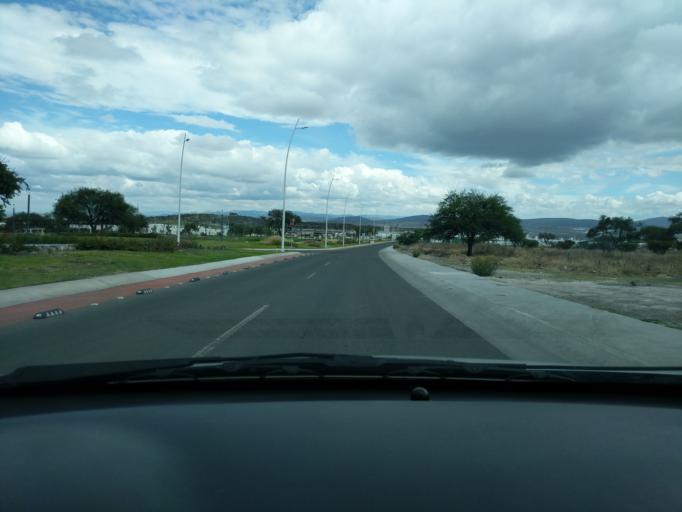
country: MX
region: Queretaro
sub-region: El Marques
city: El Pozo
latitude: 20.6540
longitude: -100.3147
